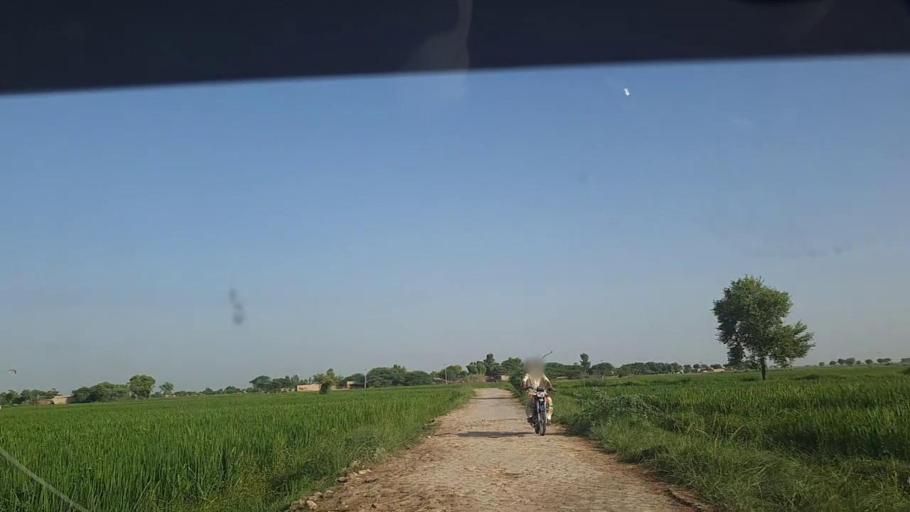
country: PK
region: Sindh
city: Tangwani
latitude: 28.2689
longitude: 69.0110
